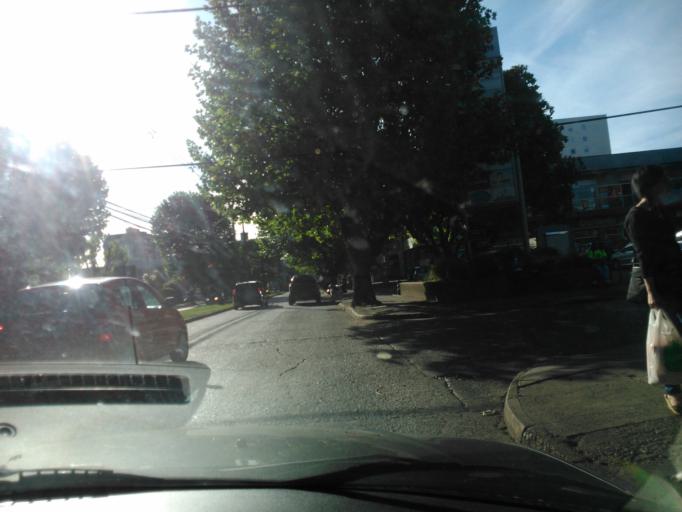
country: CL
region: Araucania
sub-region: Provincia de Cautin
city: Temuco
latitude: -38.7358
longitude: -72.6071
